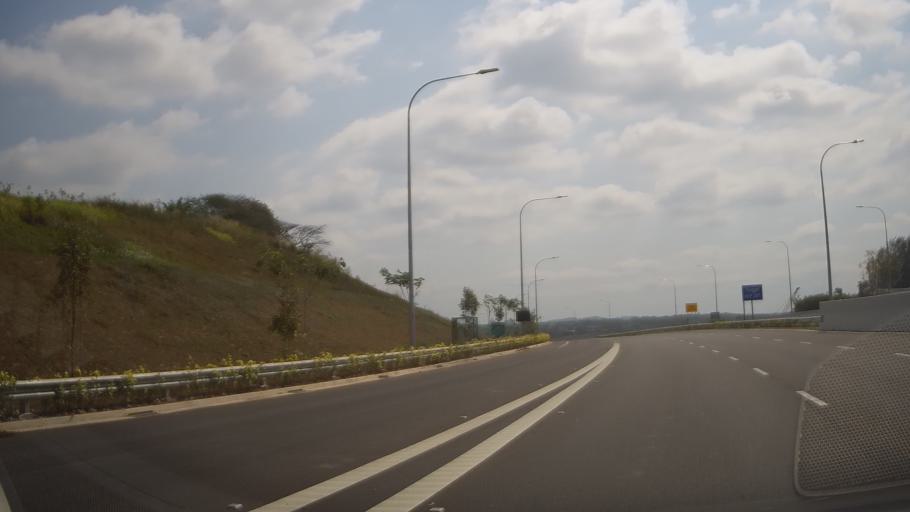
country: MY
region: Johor
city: Kampung Pasir Gudang Baru
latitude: 1.3851
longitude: 103.9199
